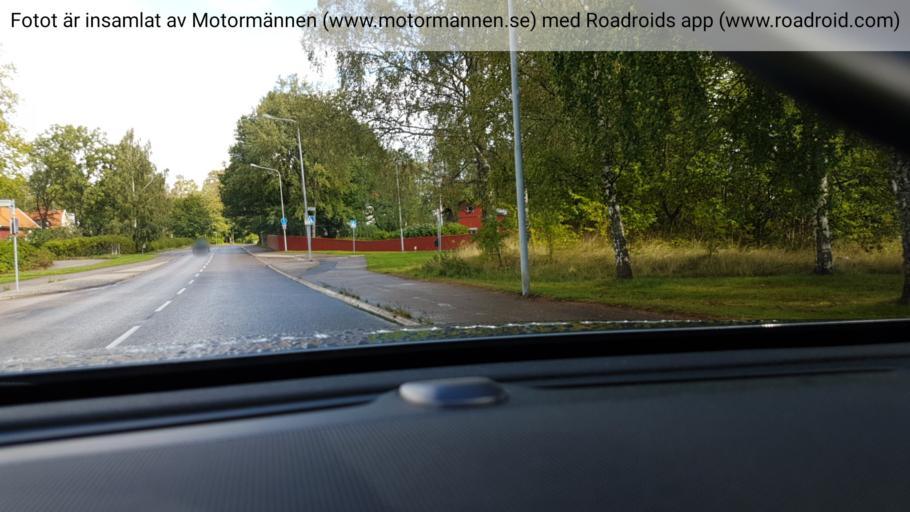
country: SE
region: Vaestra Goetaland
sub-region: Vanersborgs Kommun
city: Vanersborg
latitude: 58.3718
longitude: 12.2861
